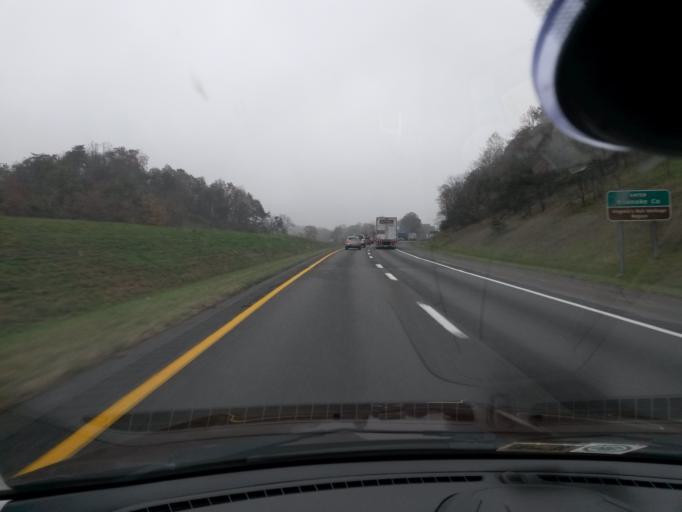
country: US
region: Virginia
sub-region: Montgomery County
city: Shawsville
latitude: 37.2476
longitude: -80.2062
